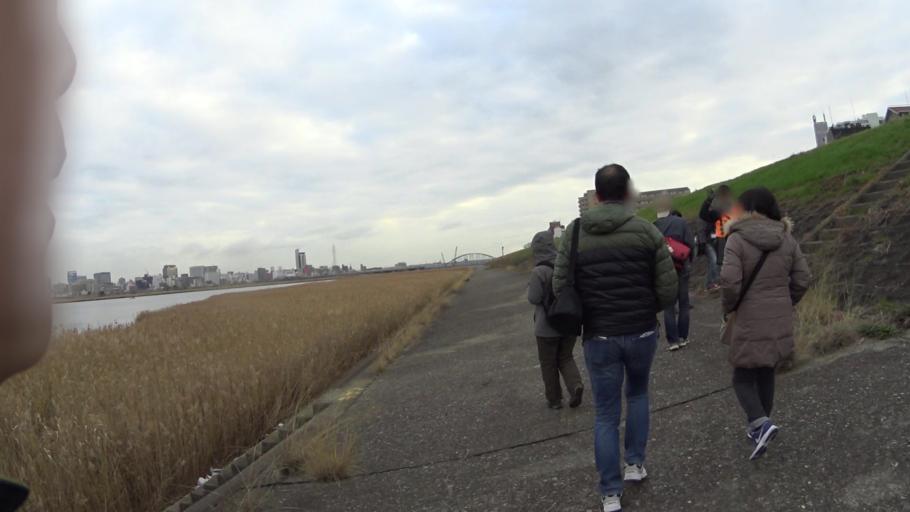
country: JP
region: Osaka
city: Osaka-shi
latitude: 34.7125
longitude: 135.4895
